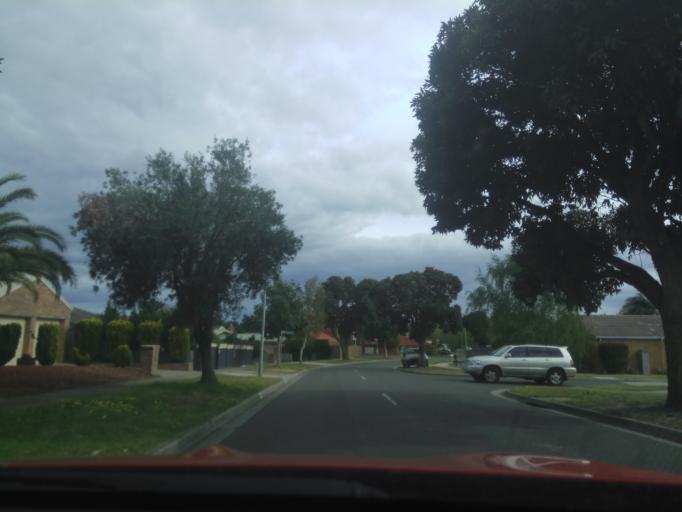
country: AU
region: Victoria
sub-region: Casey
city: Cranbourne North
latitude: -38.0728
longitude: 145.2759
